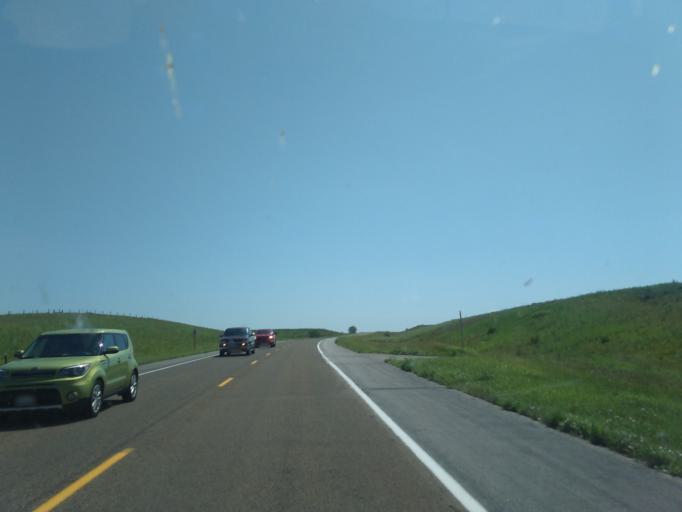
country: US
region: Nebraska
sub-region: Hitchcock County
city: Trenton
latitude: 40.1761
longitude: -101.1344
